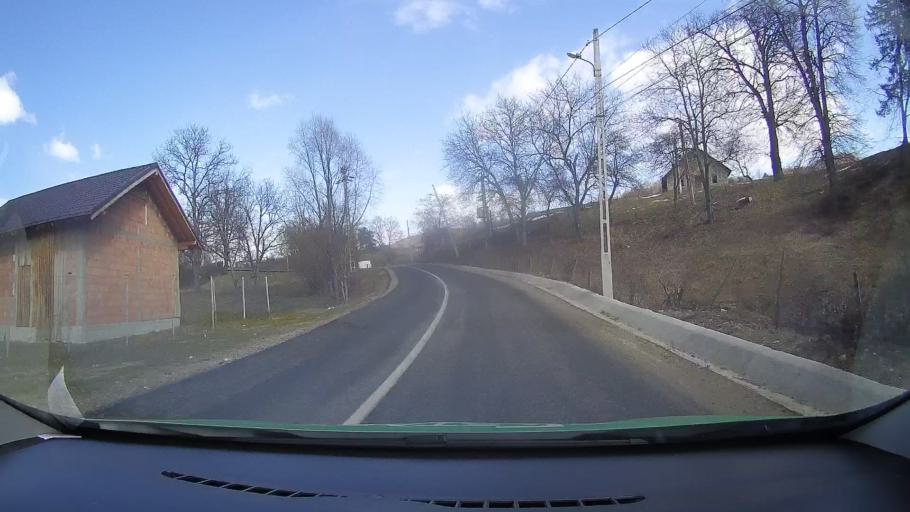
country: RO
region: Dambovita
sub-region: Comuna Fieni
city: Fieni
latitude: 45.1370
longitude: 25.4027
